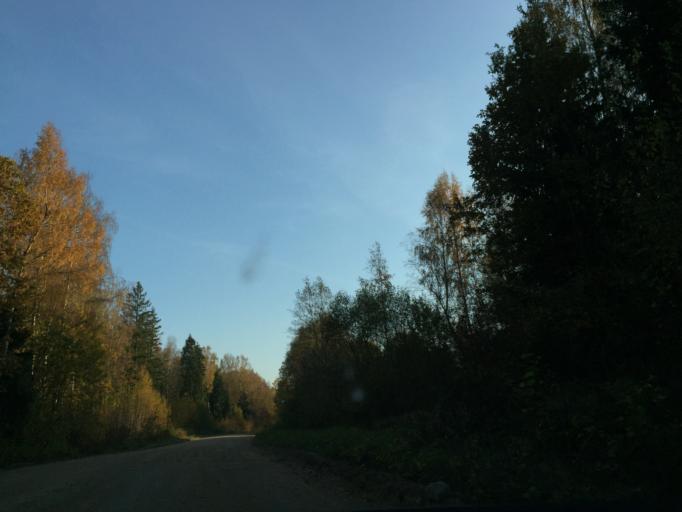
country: LV
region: Vainode
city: Vainode
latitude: 56.5925
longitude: 21.8364
